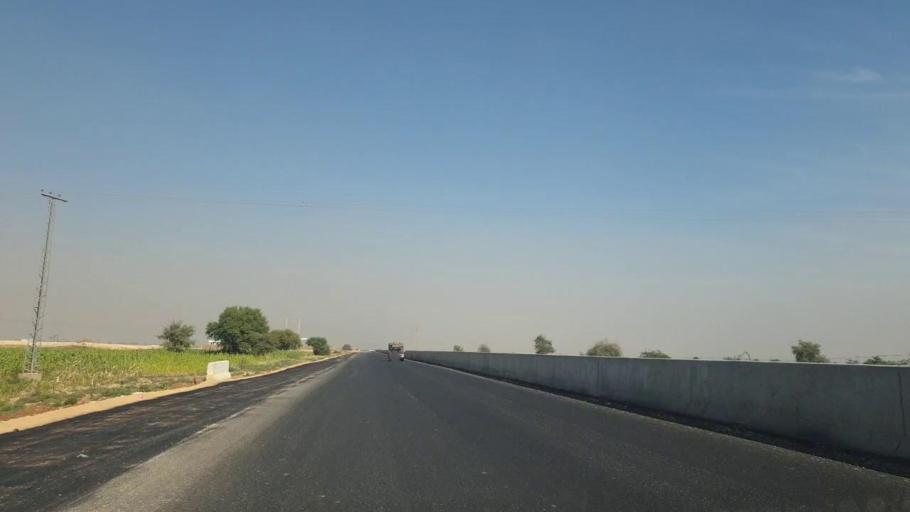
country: PK
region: Sindh
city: Jamshoro
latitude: 25.5319
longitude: 68.2819
